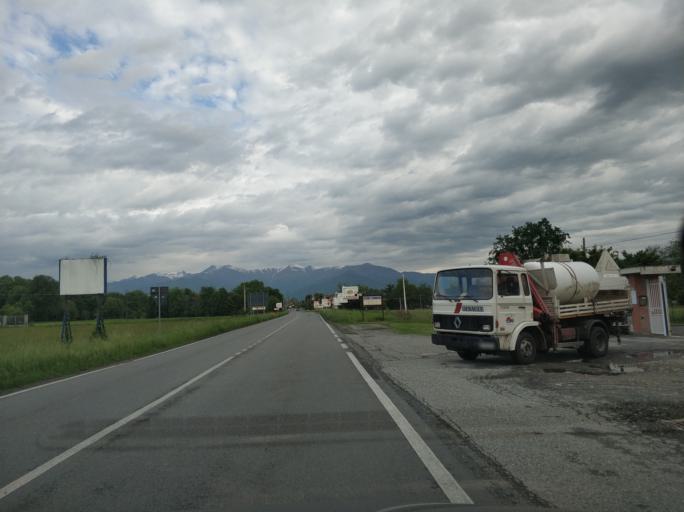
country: IT
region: Piedmont
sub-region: Provincia di Torino
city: San Maurizio
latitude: 45.2254
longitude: 7.6200
